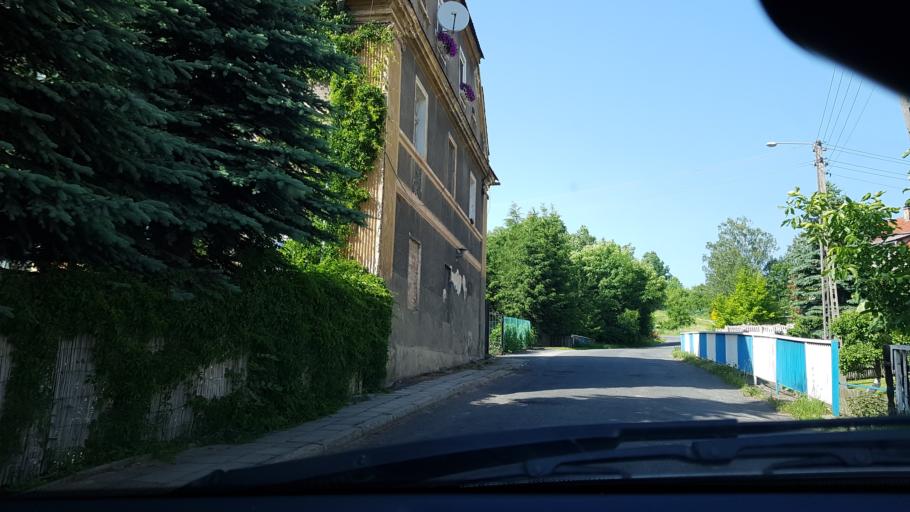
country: PL
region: Lower Silesian Voivodeship
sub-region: Powiat klodzki
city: Bozkow
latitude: 50.5113
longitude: 16.6439
